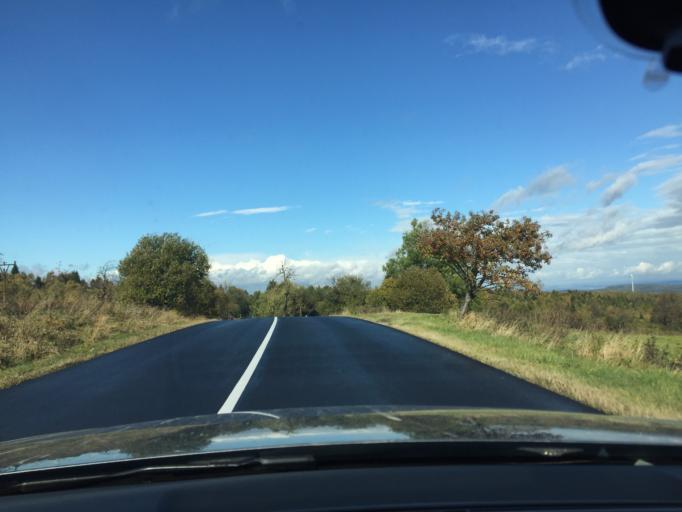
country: CZ
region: Ustecky
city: Libouchec
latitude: 50.7533
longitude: 13.9778
